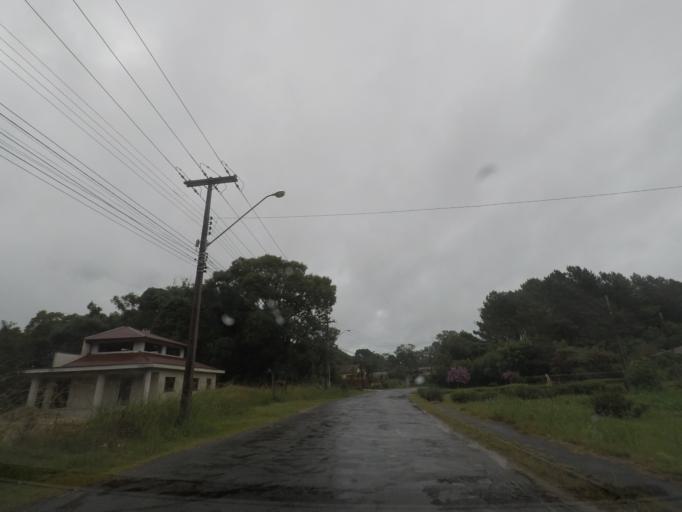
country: BR
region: Parana
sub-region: Campo Largo
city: Campo Largo
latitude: -25.4599
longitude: -49.4253
